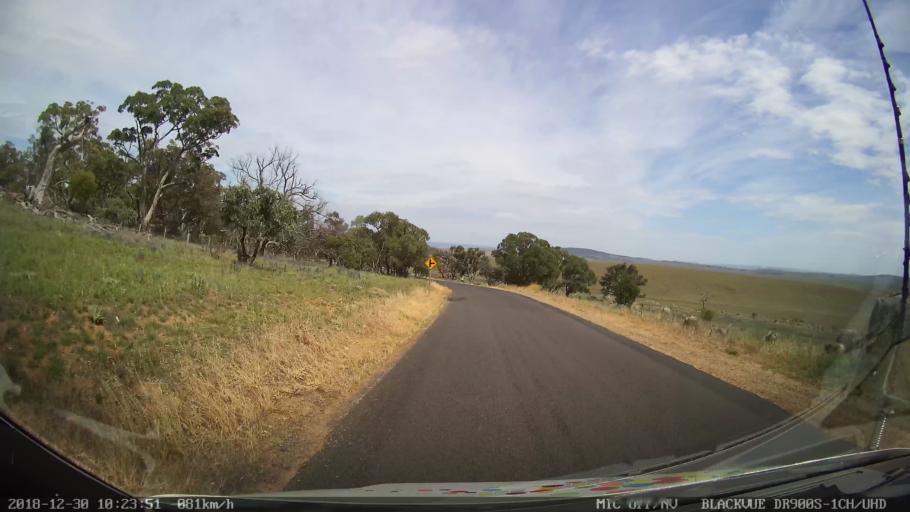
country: AU
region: New South Wales
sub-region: Snowy River
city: Berridale
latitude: -36.5338
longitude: 148.9781
